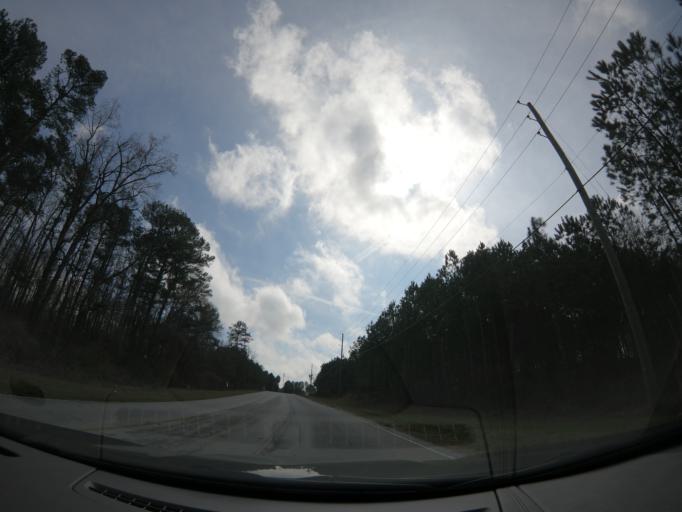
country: US
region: Georgia
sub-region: Fulton County
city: College Park
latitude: 33.6367
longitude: -84.4681
